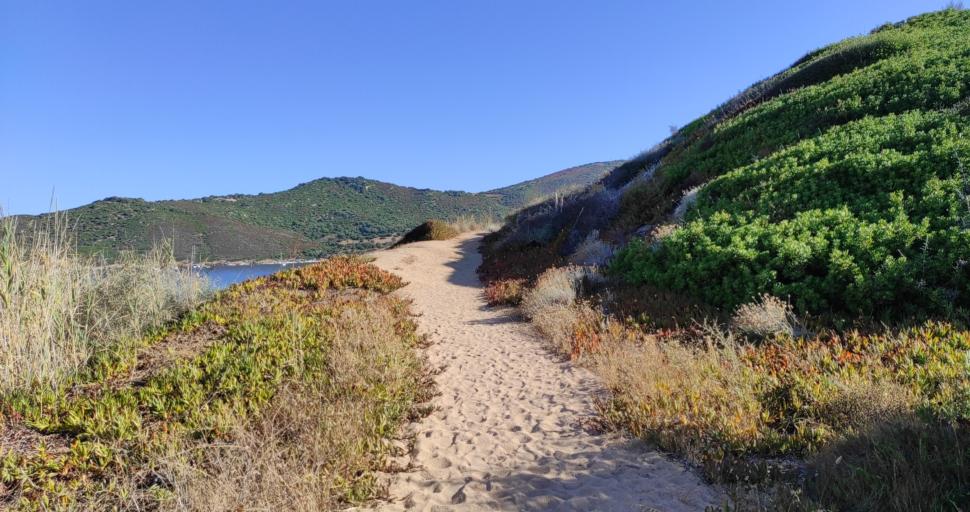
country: FR
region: Corsica
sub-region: Departement de la Corse-du-Sud
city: Alata
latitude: 41.9831
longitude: 8.6696
